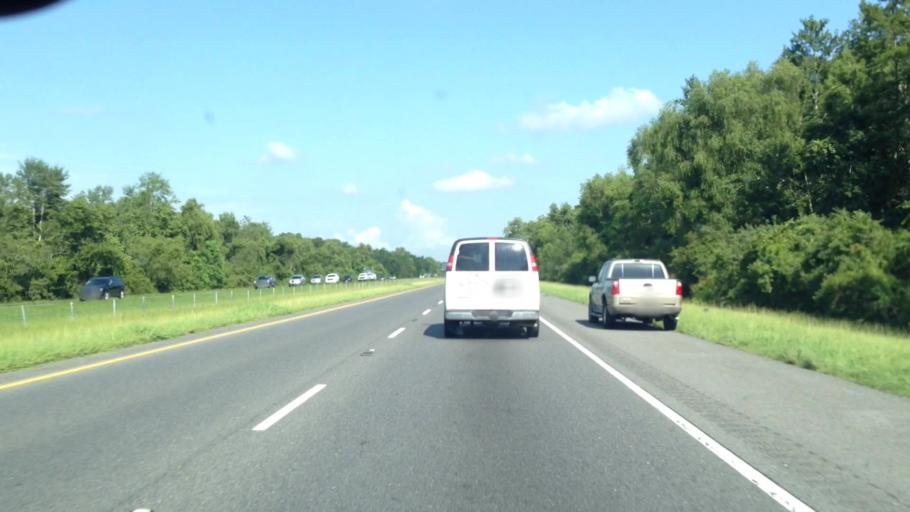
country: US
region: Louisiana
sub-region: Saint James Parish
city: Grand Point
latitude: 30.1419
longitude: -90.7533
